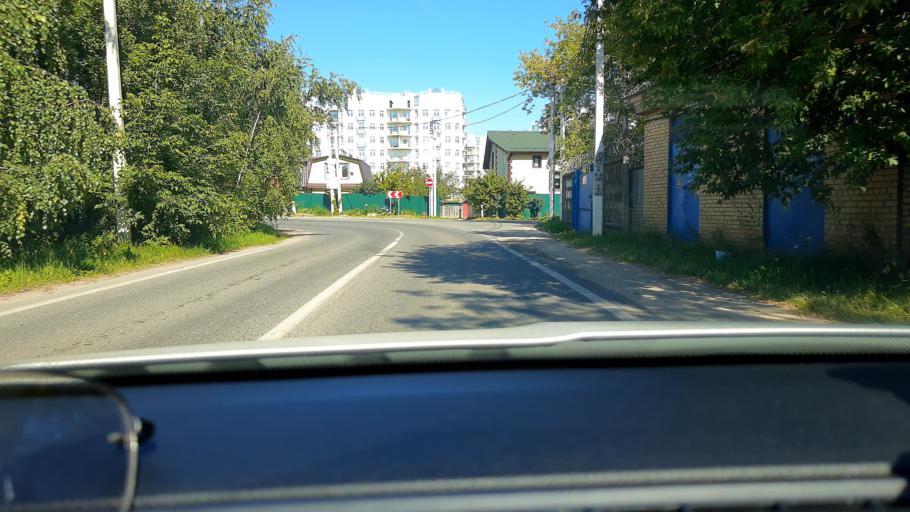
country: RU
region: Moskovskaya
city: Petrovo-Dal'neye
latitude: 55.7717
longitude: 37.2212
